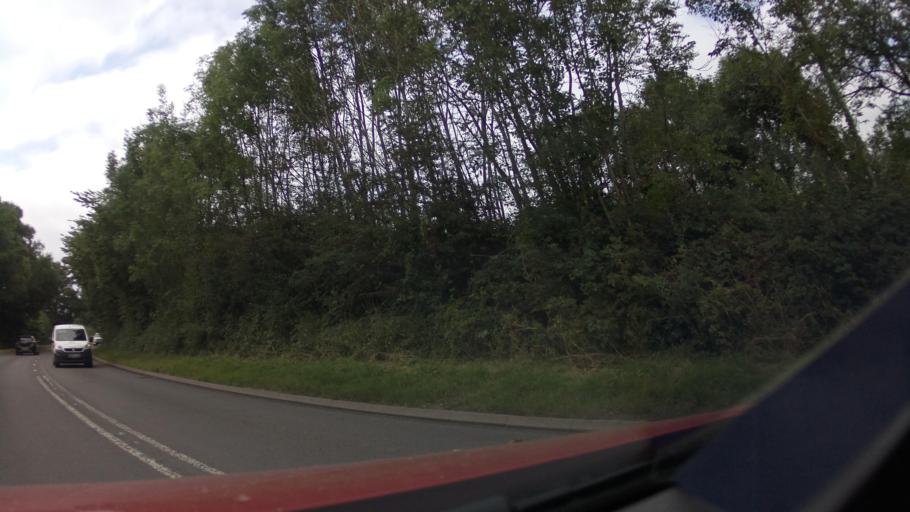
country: GB
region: England
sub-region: Staffordshire
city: Mayfield
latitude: 53.0132
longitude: -1.7739
